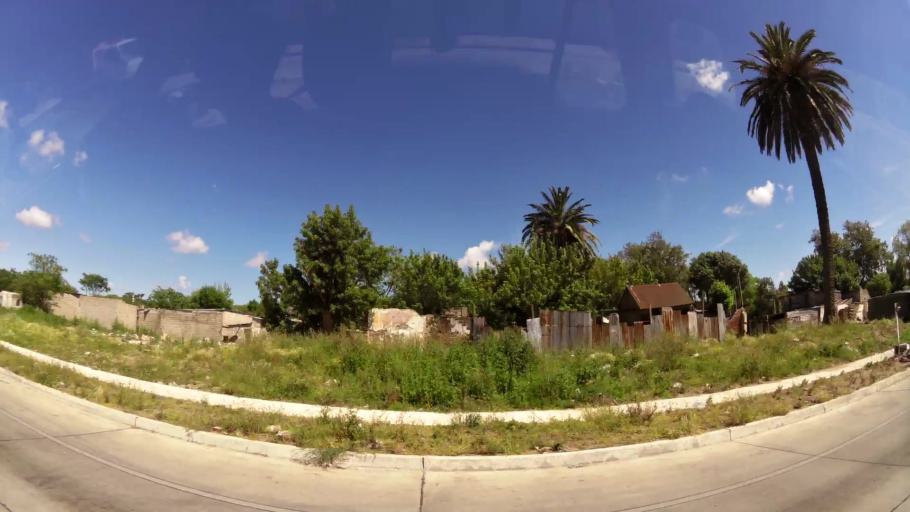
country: UY
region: Montevideo
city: Montevideo
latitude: -34.8450
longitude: -56.1447
